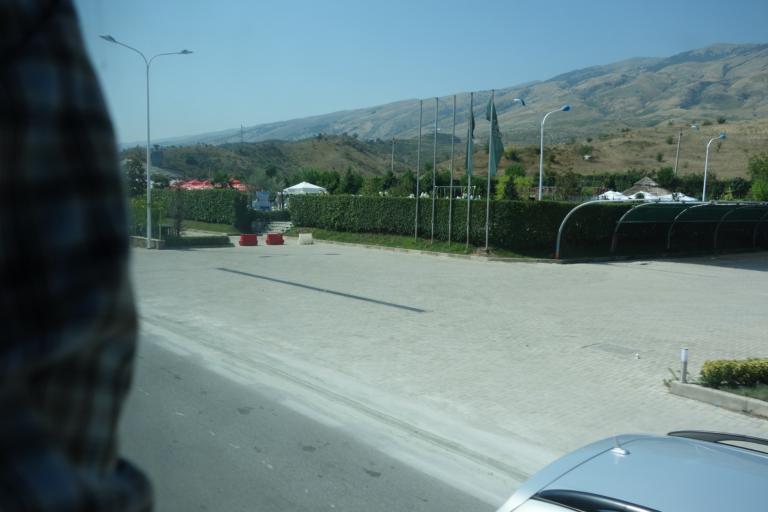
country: AL
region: Gjirokaster
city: Gjirokaster
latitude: 40.1199
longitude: 20.1153
